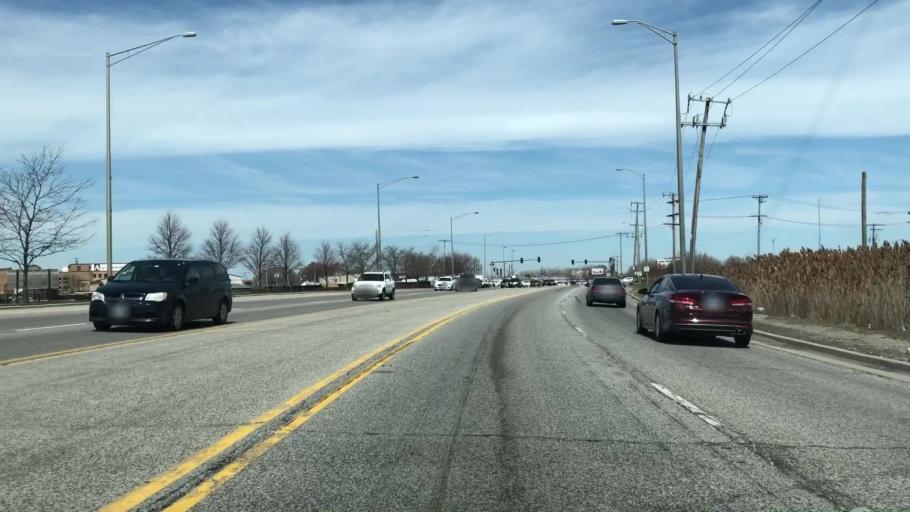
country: US
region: Illinois
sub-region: Cook County
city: Summit
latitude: 41.7726
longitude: -87.8042
